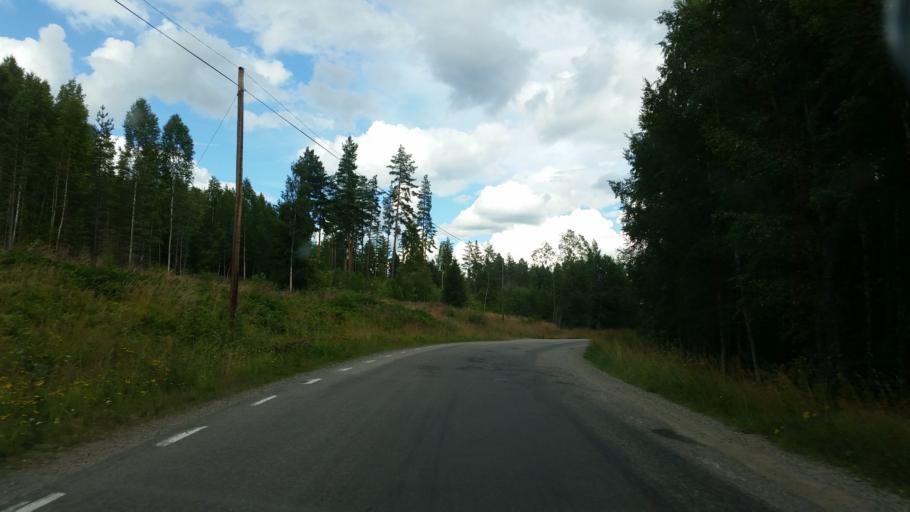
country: SE
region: Gaevleborg
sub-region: Hudiksvalls Kommun
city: Delsbo
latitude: 61.9165
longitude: 16.5944
